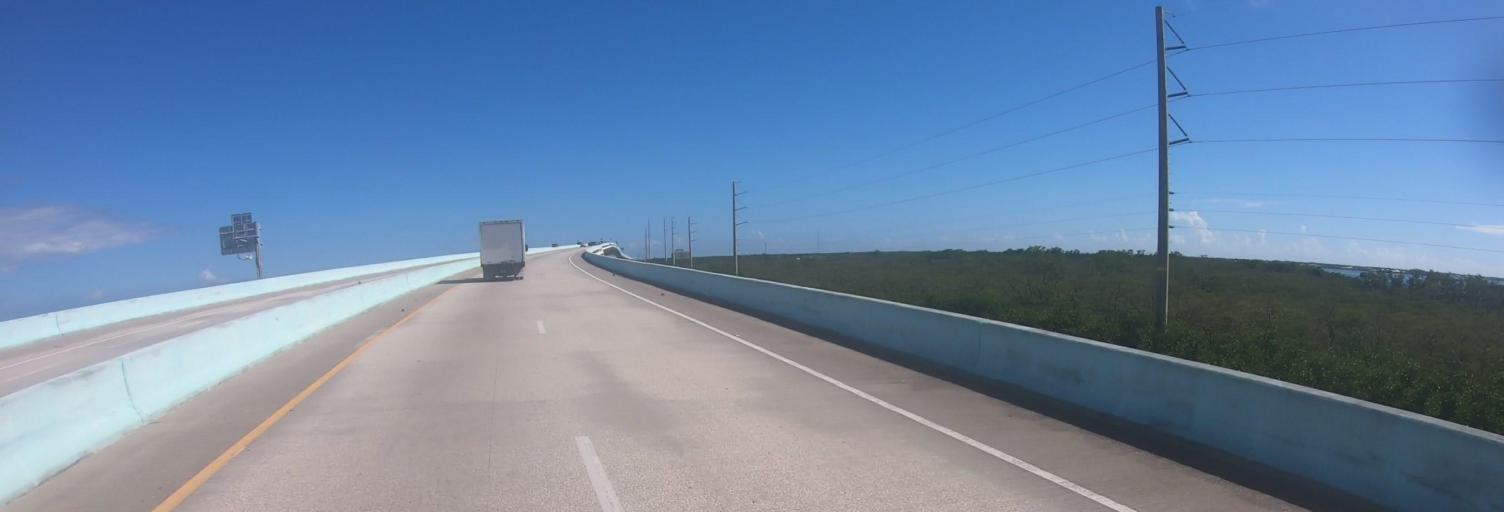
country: US
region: Florida
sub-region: Monroe County
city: North Key Largo
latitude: 25.1884
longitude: -80.3935
